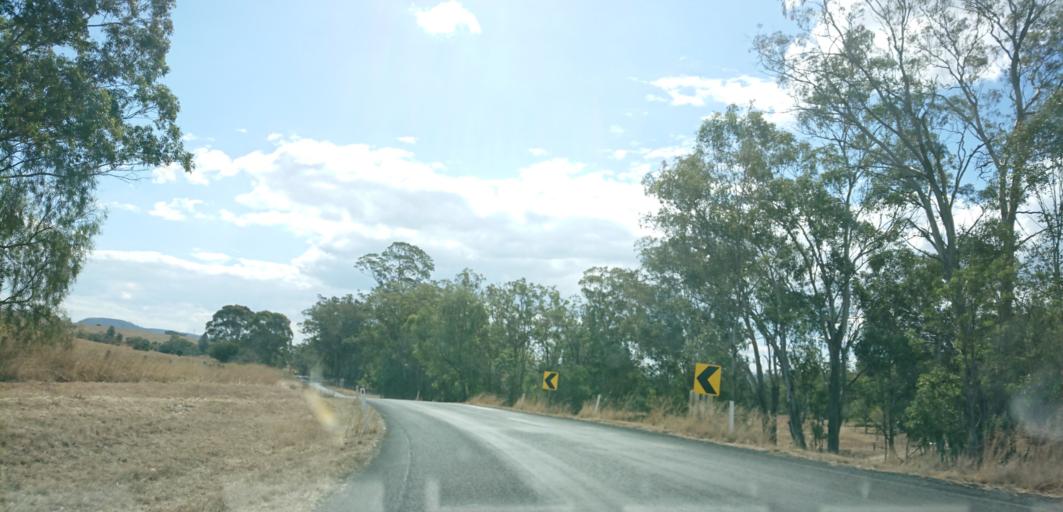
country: AU
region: Queensland
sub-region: Toowoomba
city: Top Camp
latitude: -27.7956
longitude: 152.1045
